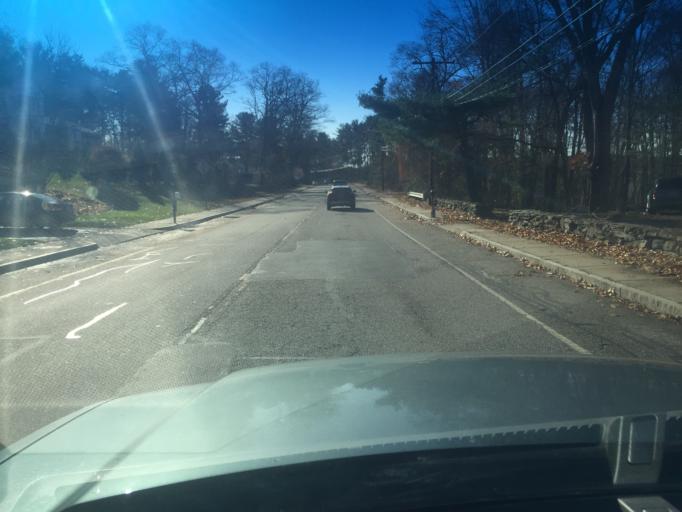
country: US
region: Massachusetts
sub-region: Norfolk County
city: Franklin
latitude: 42.0966
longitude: -71.4272
